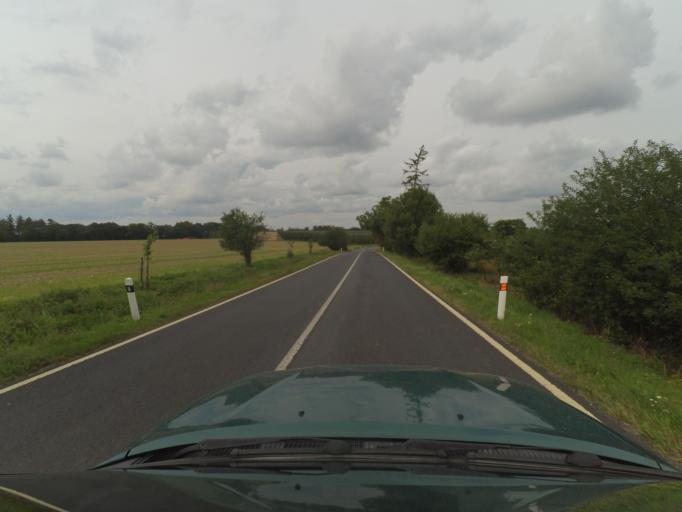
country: CZ
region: Central Bohemia
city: Revnicov
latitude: 50.2397
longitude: 13.7594
